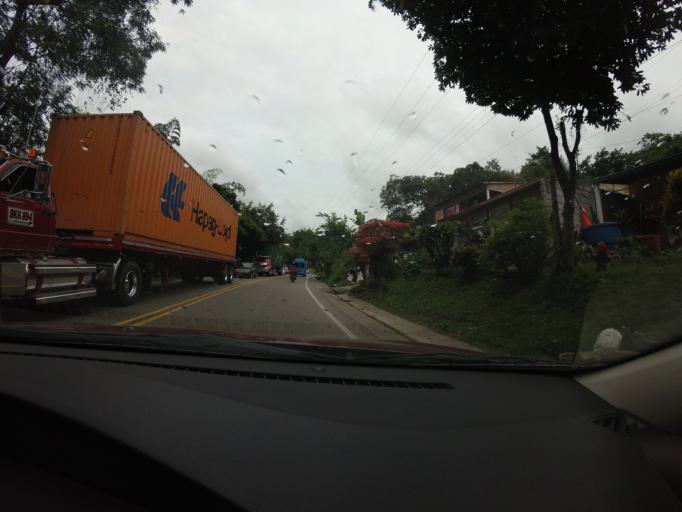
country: CO
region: Cundinamarca
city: Guaduas
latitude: 5.0628
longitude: -74.5899
